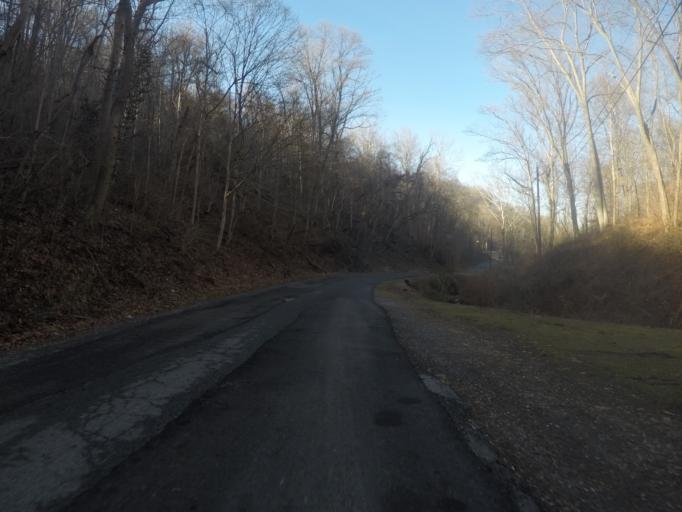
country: US
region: West Virginia
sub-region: Cabell County
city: Huntington
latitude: 38.3941
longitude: -82.4866
